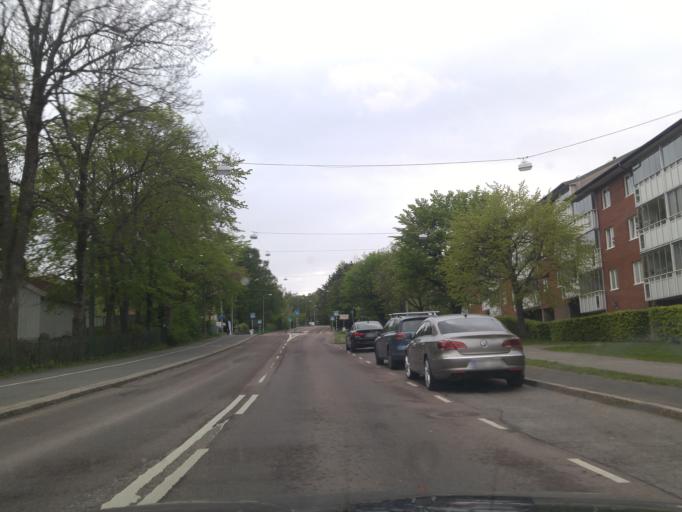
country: SE
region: Vaestra Goetaland
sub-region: Goteborg
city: Majorna
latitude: 57.6681
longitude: 11.9333
